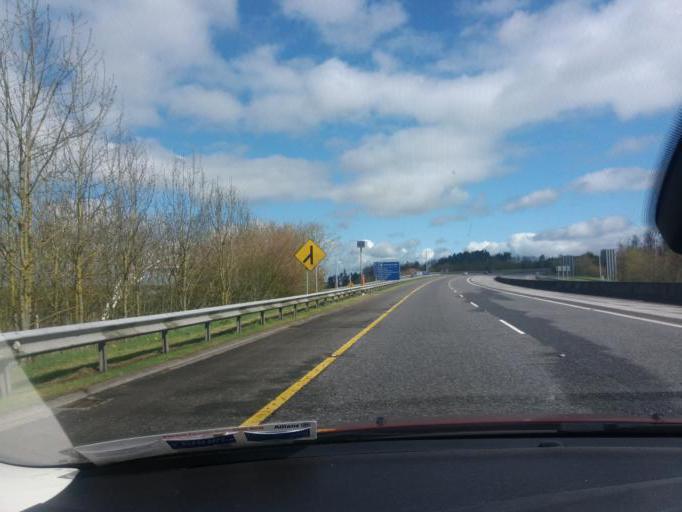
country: IE
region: Munster
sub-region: County Cork
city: Fermoy
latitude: 52.1155
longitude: -8.2728
